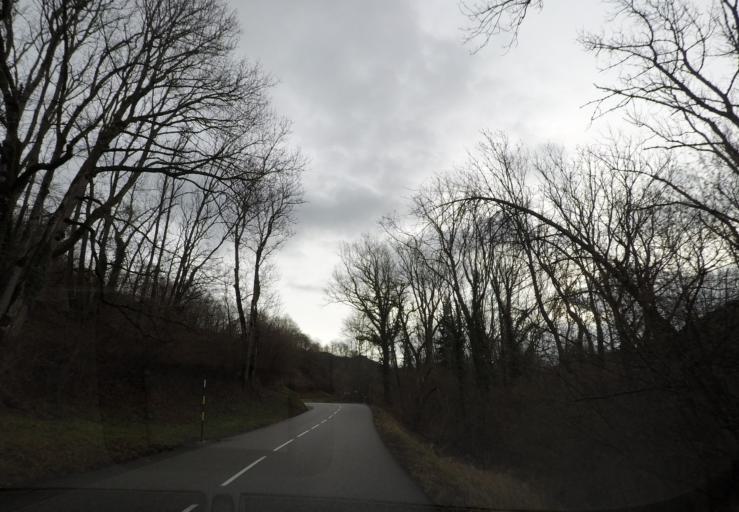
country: FR
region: Rhone-Alpes
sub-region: Departement de la Haute-Savoie
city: Chatillon-sur-Cluses
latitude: 46.0767
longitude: 6.5979
